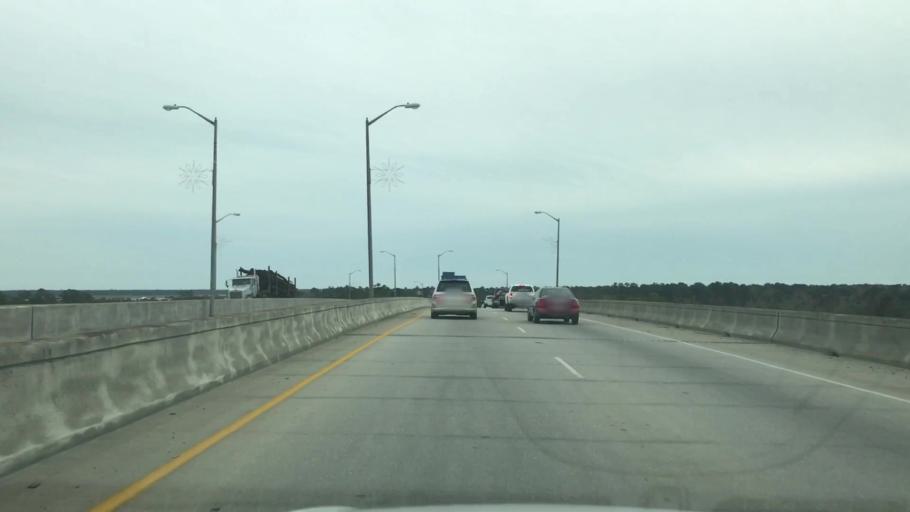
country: US
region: South Carolina
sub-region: Georgetown County
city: Georgetown
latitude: 33.3586
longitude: -79.2946
